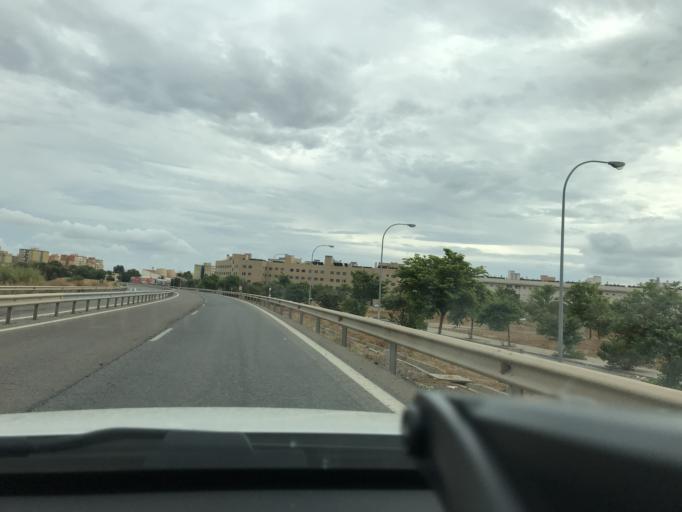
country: ES
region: Andalusia
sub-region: Provincia de Sevilla
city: Sevilla
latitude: 37.4299
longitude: -5.9654
